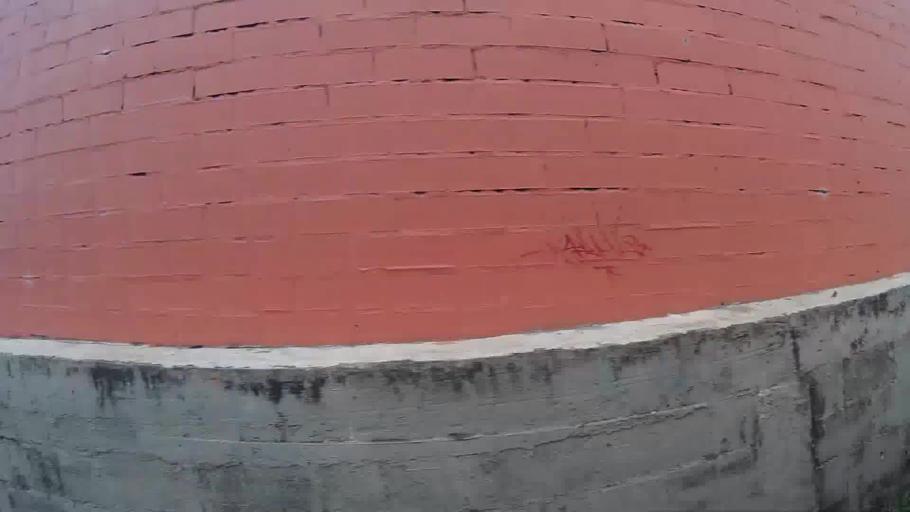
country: CO
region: Valle del Cauca
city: Ulloa
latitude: 4.7314
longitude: -75.7185
